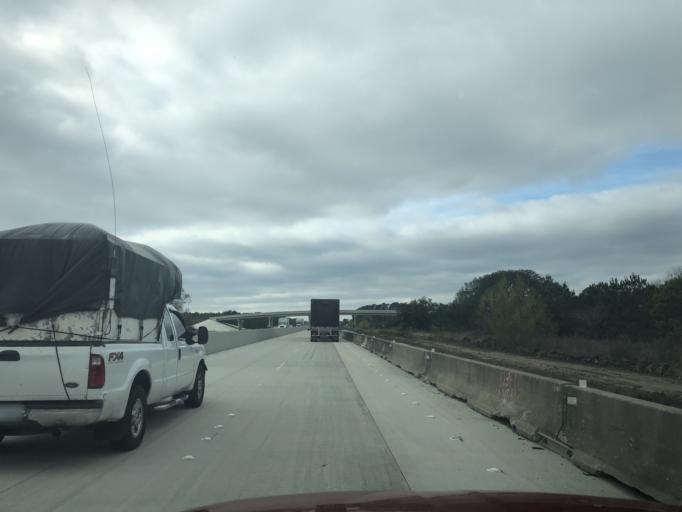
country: US
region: Texas
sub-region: Chambers County
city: Winnie
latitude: 29.8659
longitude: -94.3489
